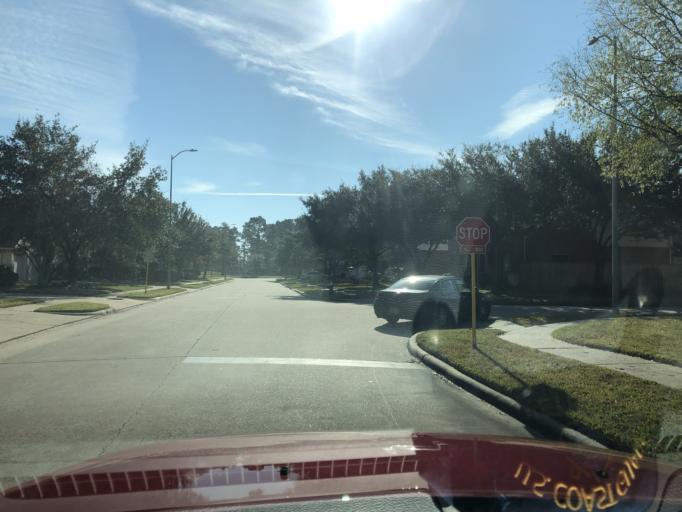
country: US
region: Texas
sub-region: Harris County
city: Tomball
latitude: 30.0308
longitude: -95.5629
